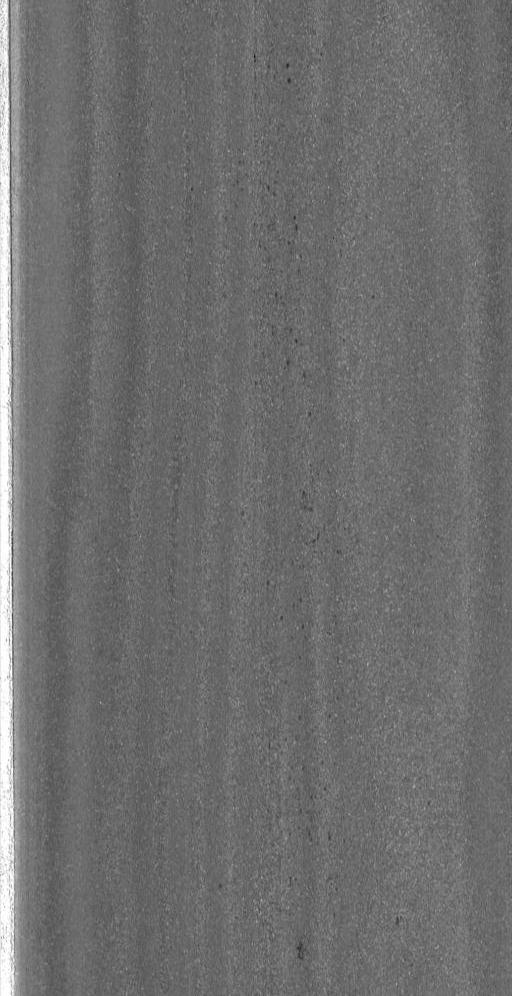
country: US
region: Vermont
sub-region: Caledonia County
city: Saint Johnsbury
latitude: 44.3000
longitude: -72.0557
